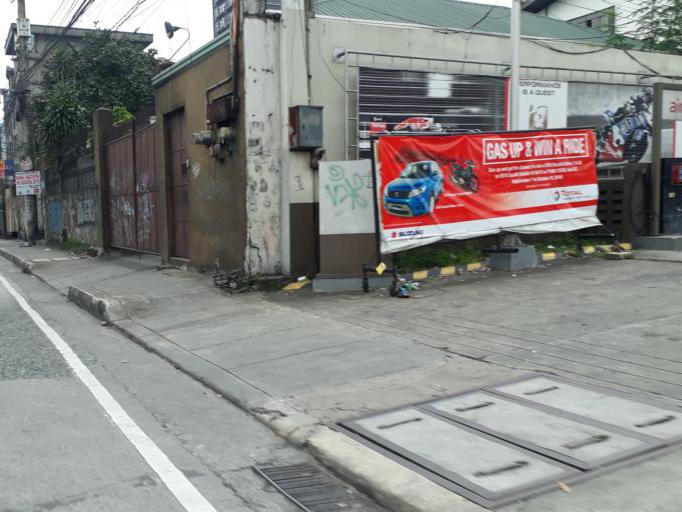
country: PH
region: Calabarzon
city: Bagong Pagasa
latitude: 14.6583
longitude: 121.0357
